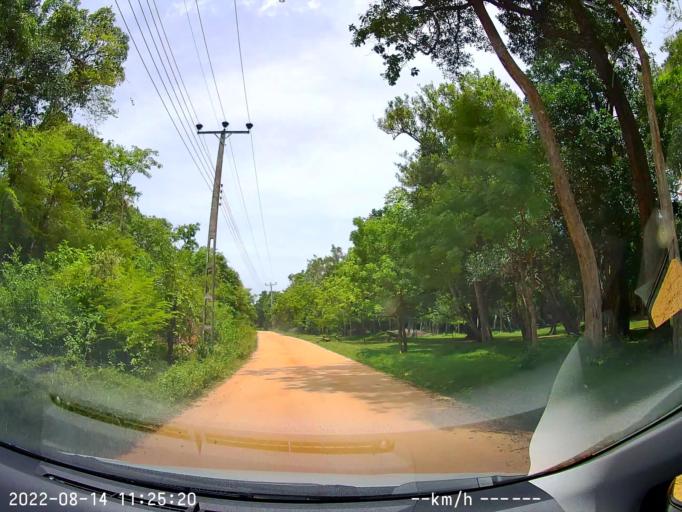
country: LK
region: Central
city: Sigiriya
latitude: 7.9690
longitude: 80.7609
